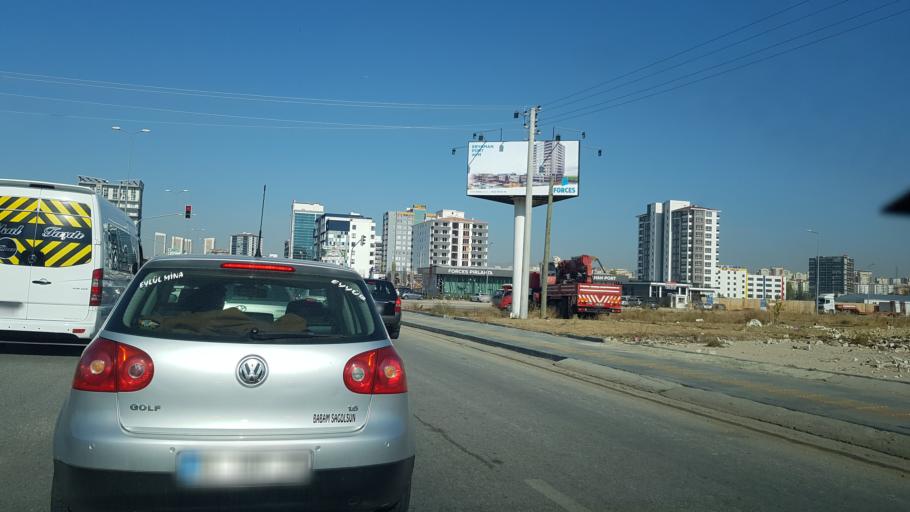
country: TR
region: Ankara
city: Etimesgut
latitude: 39.9636
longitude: 32.6067
